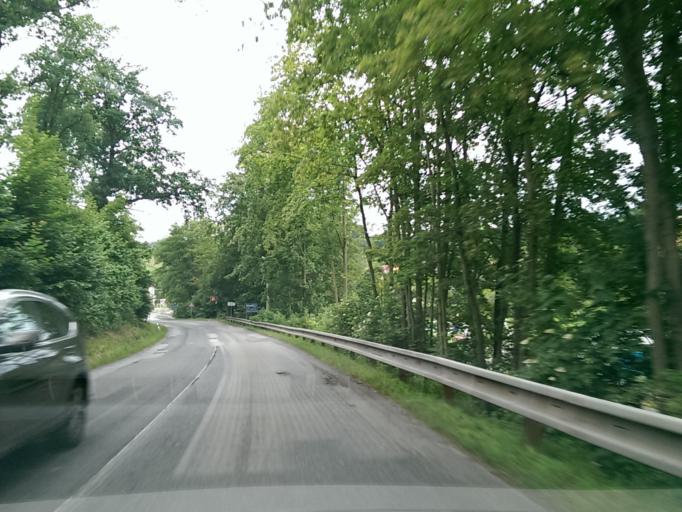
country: CZ
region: Liberecky
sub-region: Okres Semily
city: Turnov
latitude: 50.5906
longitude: 15.1867
